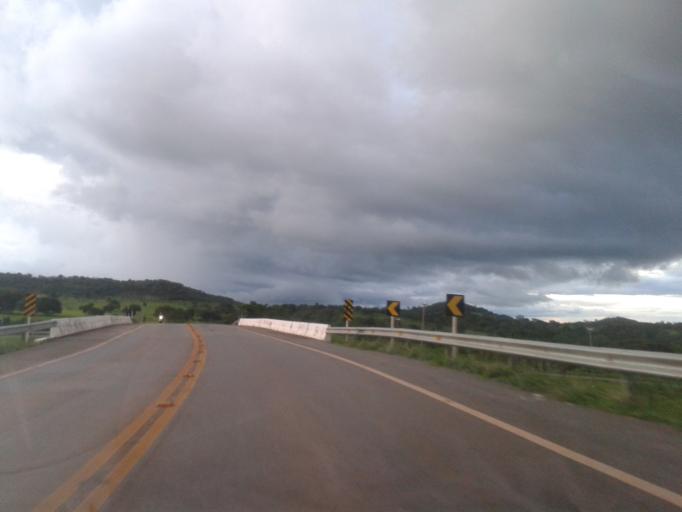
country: BR
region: Goias
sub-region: Morrinhos
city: Morrinhos
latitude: -17.7275
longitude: -49.1539
